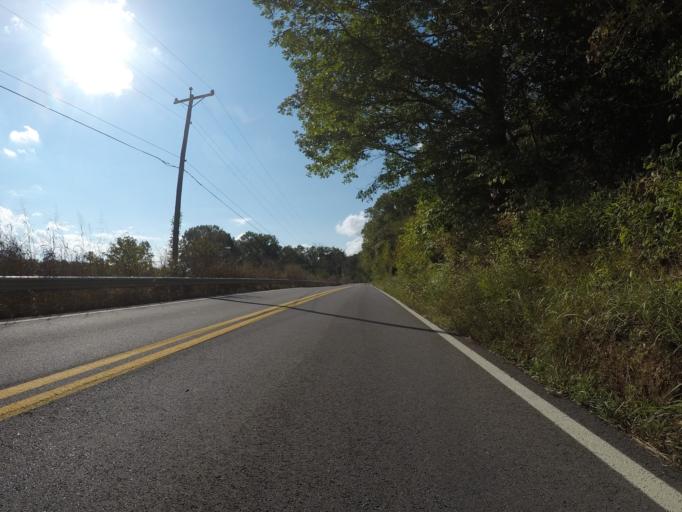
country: US
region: Ohio
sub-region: Lawrence County
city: Burlington
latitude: 38.3726
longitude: -82.5205
